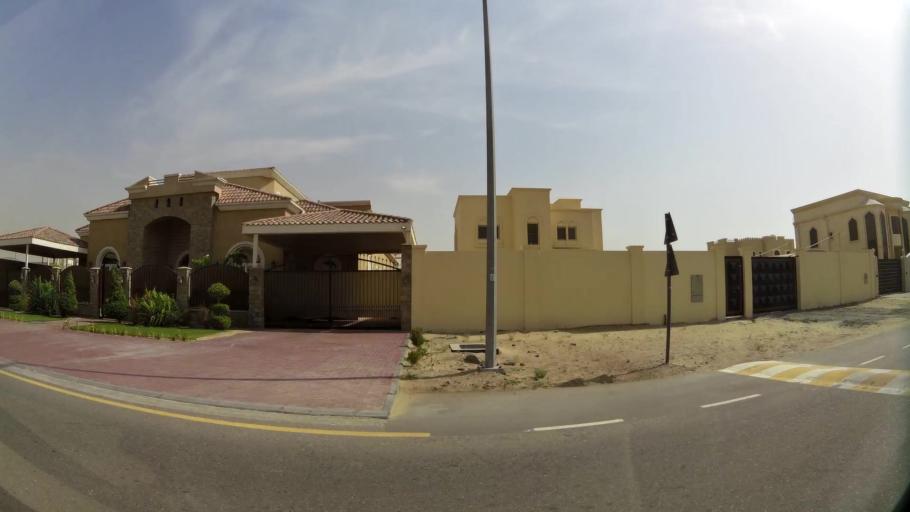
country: AE
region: Ash Shariqah
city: Sharjah
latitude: 25.2662
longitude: 55.4679
